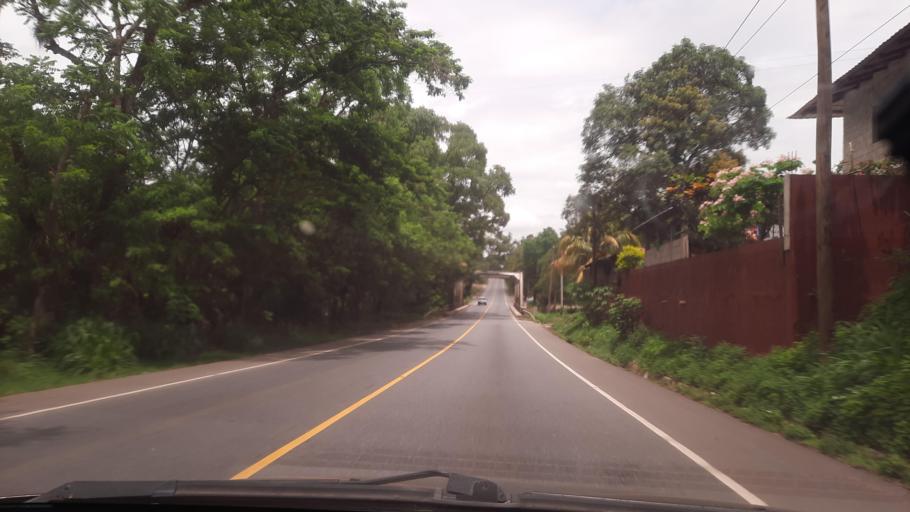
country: GT
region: Izabal
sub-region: Municipio de Los Amates
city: Los Amates
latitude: 15.2374
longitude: -89.1837
